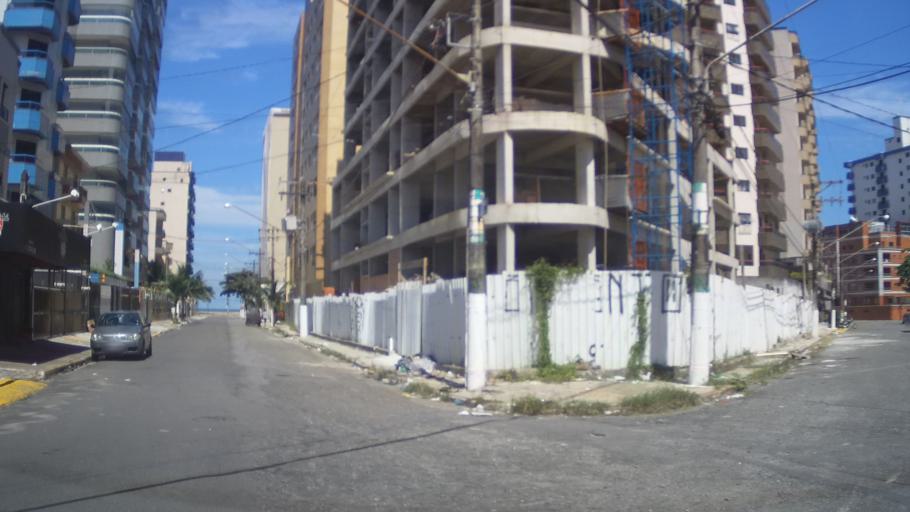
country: BR
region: Sao Paulo
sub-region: Praia Grande
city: Praia Grande
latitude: -24.0232
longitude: -46.4628
